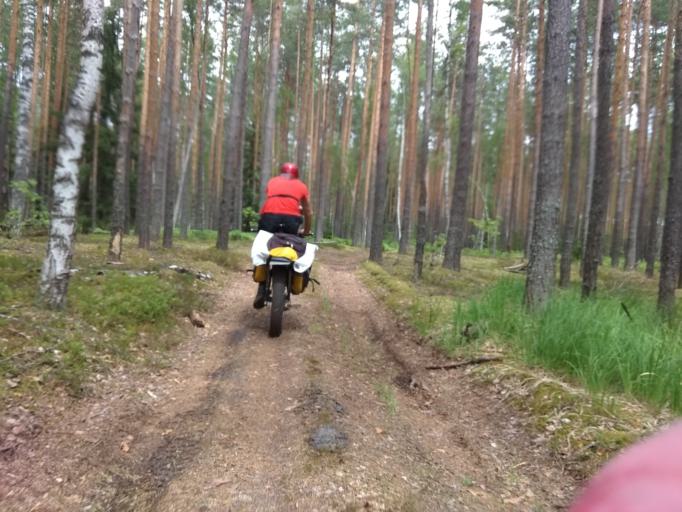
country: RU
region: Moskovskaya
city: Misheronskiy
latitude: 55.6888
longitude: 39.7109
